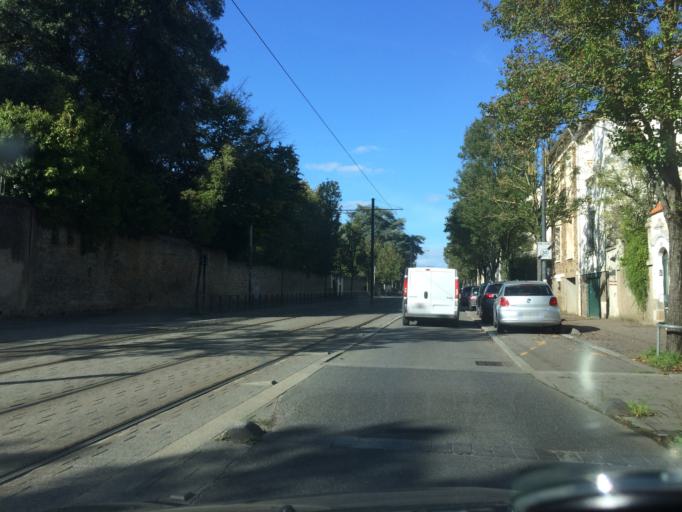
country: FR
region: Pays de la Loire
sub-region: Departement de la Loire-Atlantique
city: Nantes
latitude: 47.2355
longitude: -1.5565
